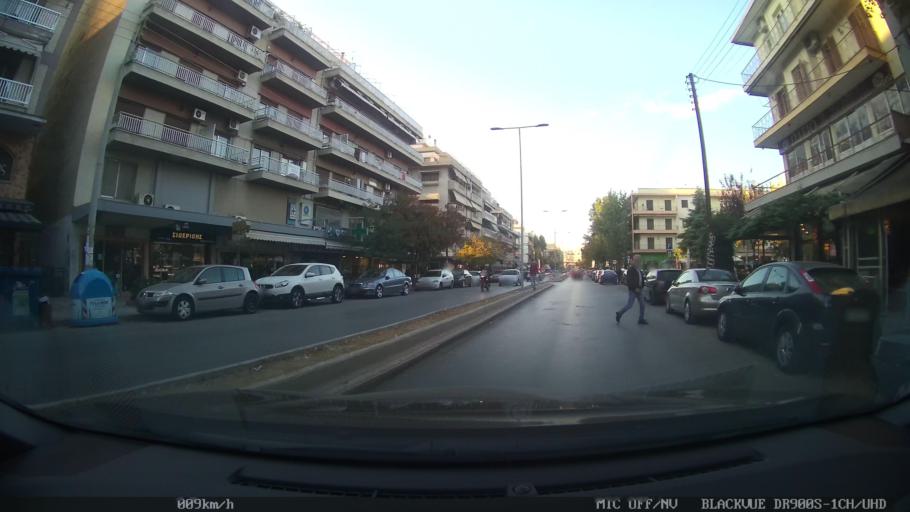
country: GR
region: Central Macedonia
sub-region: Nomos Thessalonikis
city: Triandria
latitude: 40.6025
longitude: 22.9697
